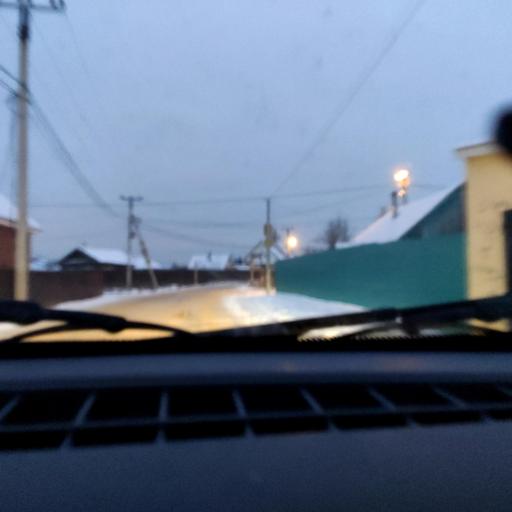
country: RU
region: Bashkortostan
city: Ufa
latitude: 54.6762
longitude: 56.0910
